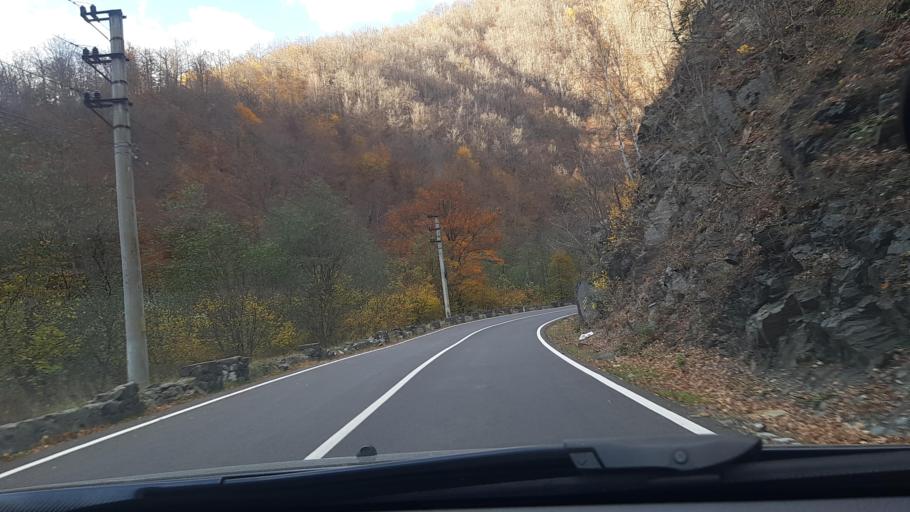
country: RO
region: Valcea
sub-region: Comuna Voineasa
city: Voineasa
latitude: 45.4058
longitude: 23.9934
